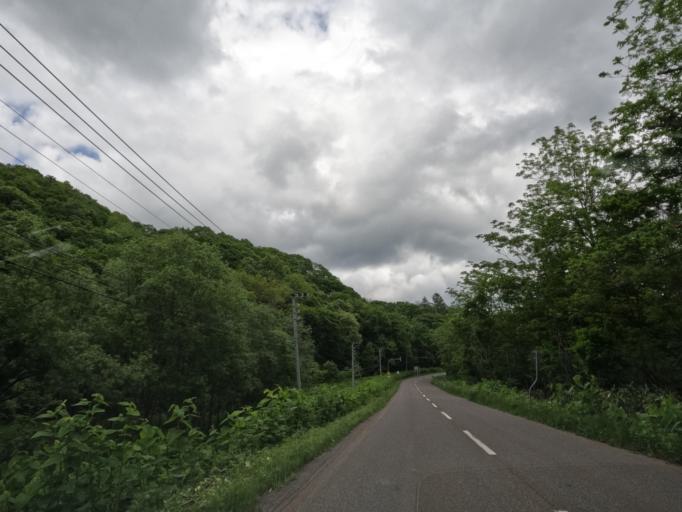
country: JP
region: Hokkaido
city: Takikawa
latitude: 43.5696
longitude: 141.7046
